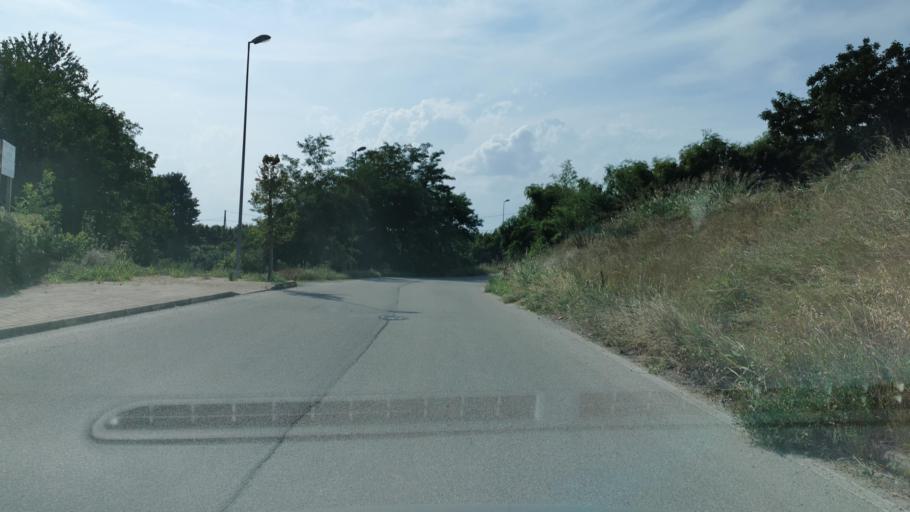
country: IT
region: Piedmont
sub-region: Provincia di Cuneo
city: La Morra
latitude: 44.6440
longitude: 7.9251
